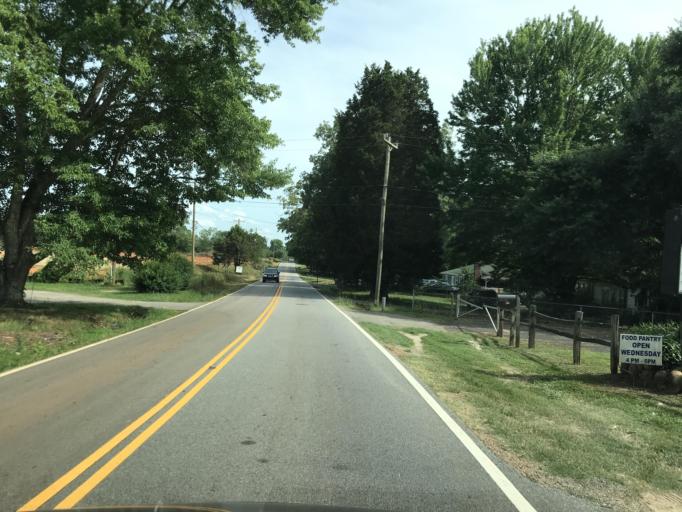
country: US
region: South Carolina
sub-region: Greenville County
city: Gantt
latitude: 34.7705
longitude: -82.4166
